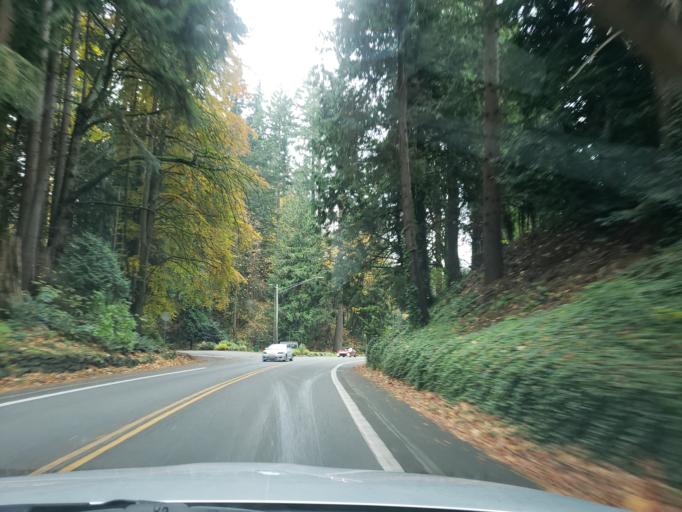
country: US
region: Washington
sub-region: Snohomish County
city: Everett
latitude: 47.9616
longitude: -122.2176
